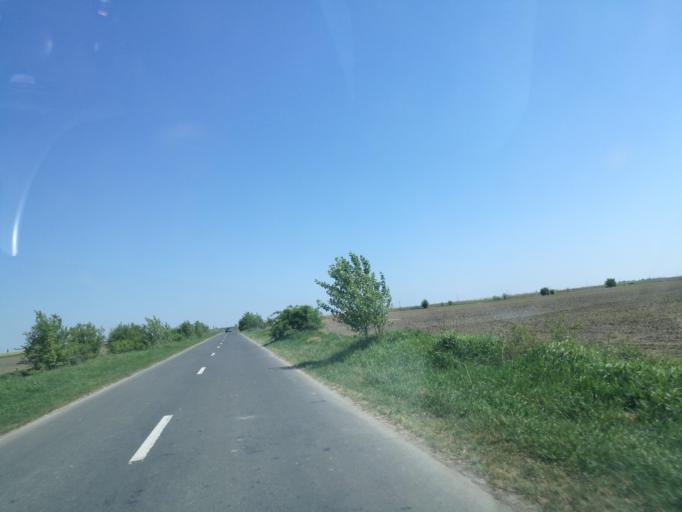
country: RO
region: Ialomita
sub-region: Comuna Adancata
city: Adancata
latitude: 44.7762
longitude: 26.4416
